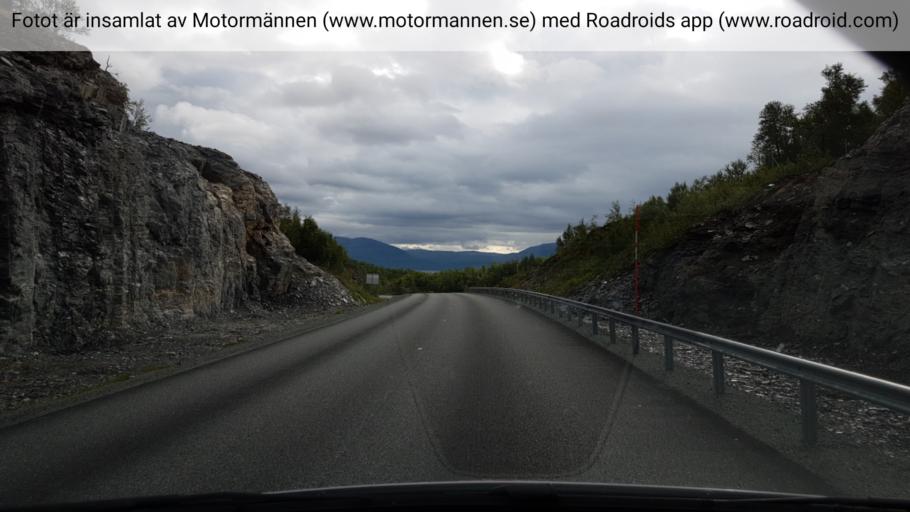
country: NO
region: Nordland
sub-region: Rana
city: Mo i Rana
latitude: 66.0507
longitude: 14.8901
